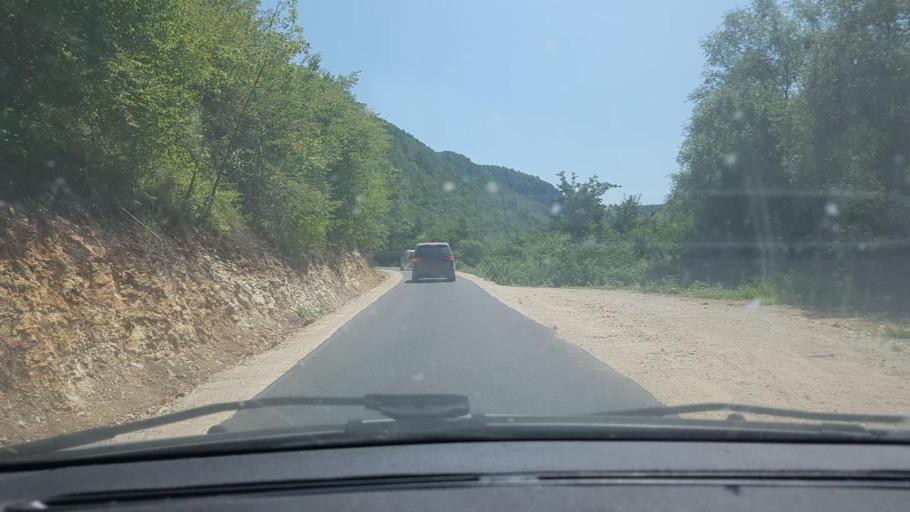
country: BA
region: Federation of Bosnia and Herzegovina
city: Orasac
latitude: 44.6234
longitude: 16.0559
